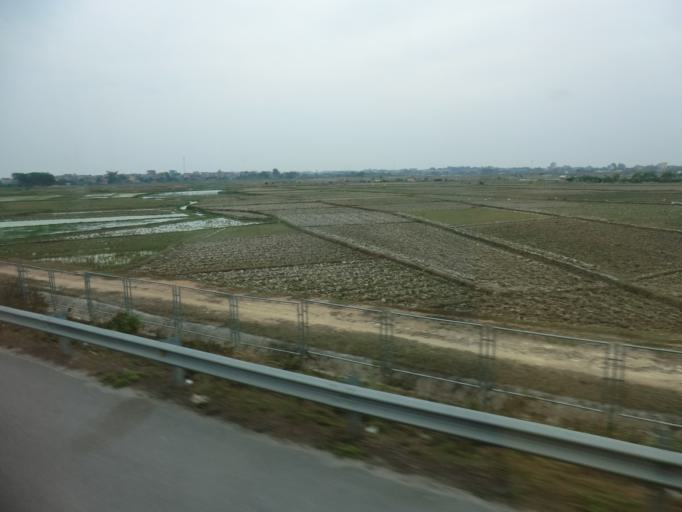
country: VN
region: Vinh Phuc
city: Phuc Yen
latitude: 21.2428
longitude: 105.7584
